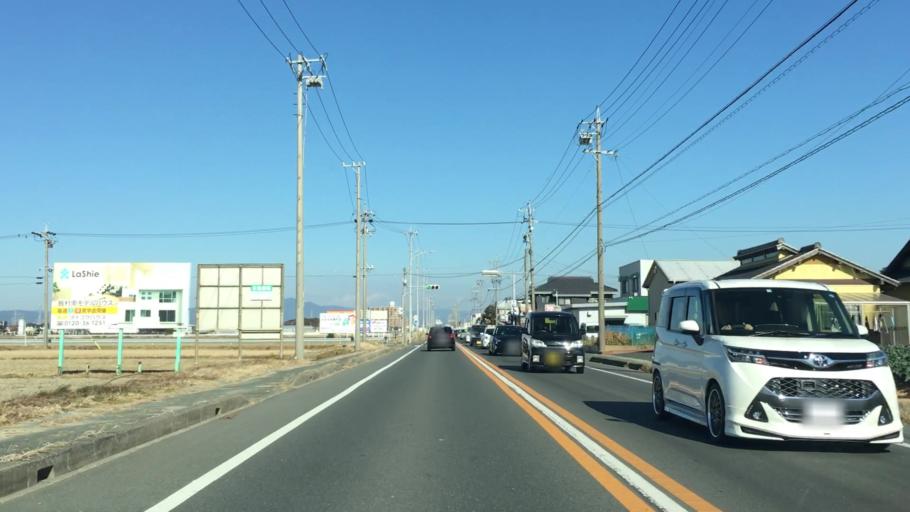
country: JP
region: Aichi
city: Toyohashi
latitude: 34.7296
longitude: 137.3580
